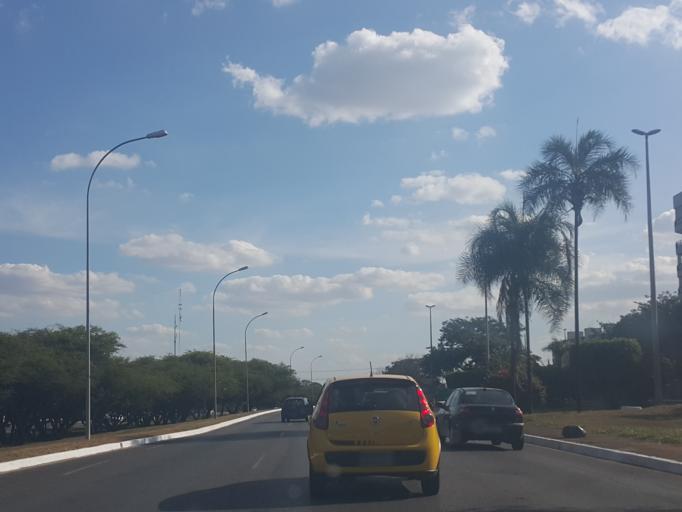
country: BR
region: Federal District
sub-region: Brasilia
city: Brasilia
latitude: -15.8056
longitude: -47.9266
